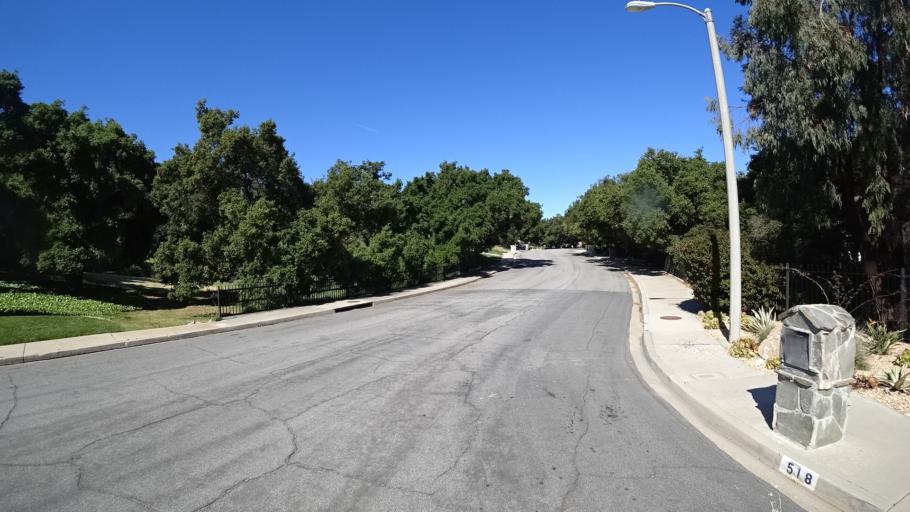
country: US
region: California
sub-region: Ventura County
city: Thousand Oaks
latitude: 34.1680
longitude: -118.8695
